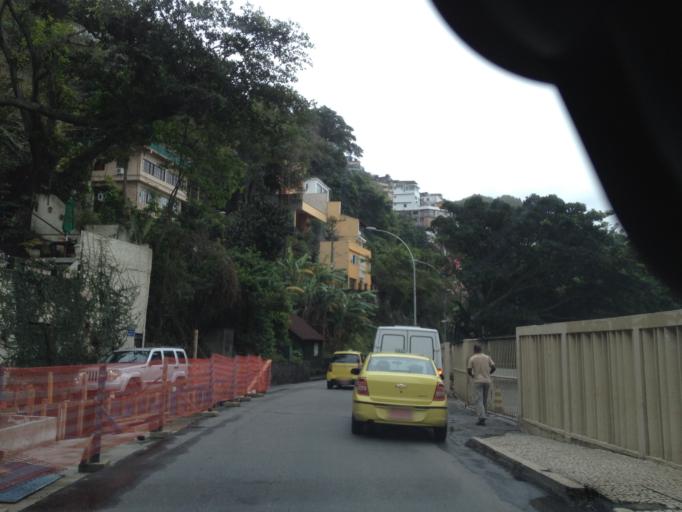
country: BR
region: Rio de Janeiro
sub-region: Rio De Janeiro
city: Rio de Janeiro
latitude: -22.9920
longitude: -43.2337
